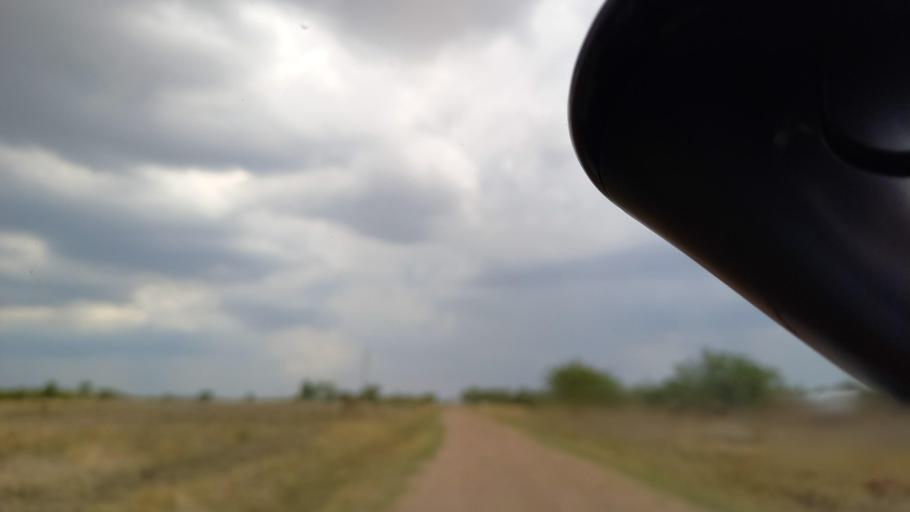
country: ZM
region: Lusaka
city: Kafue
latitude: -15.8422
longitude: 28.0921
